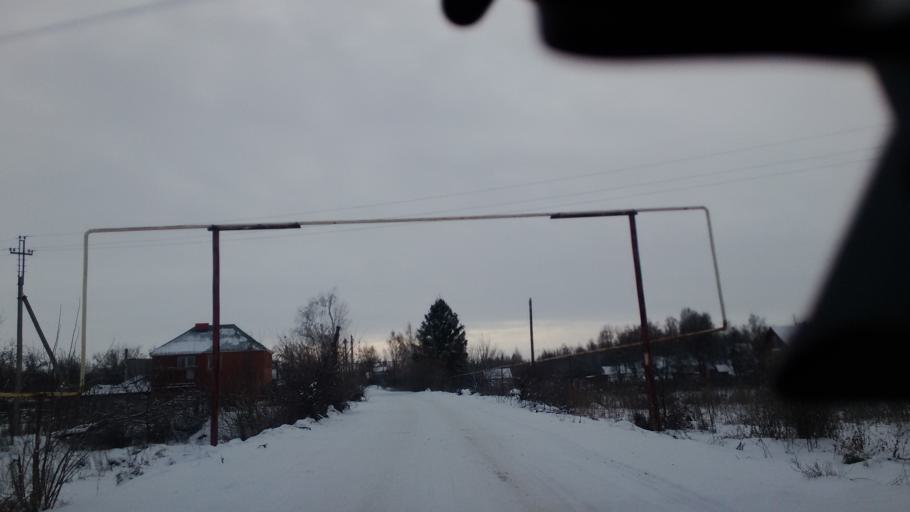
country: RU
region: Tula
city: Bogoroditsk
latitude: 53.7560
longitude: 38.1063
